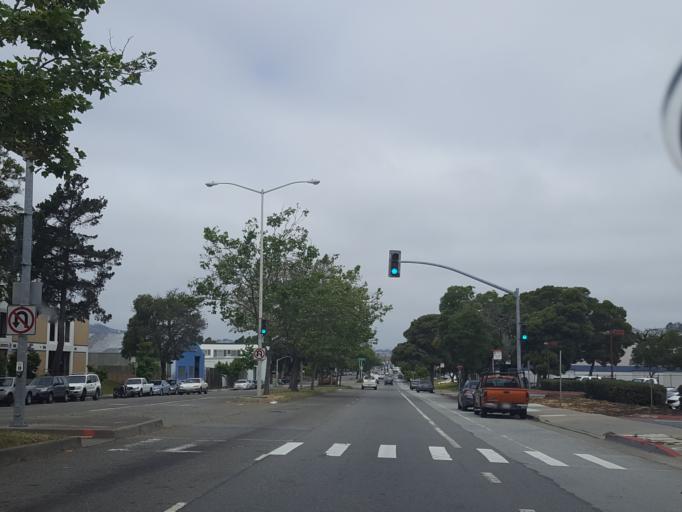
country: US
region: California
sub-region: San Francisco County
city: San Francisco
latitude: 37.7400
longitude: -122.3830
